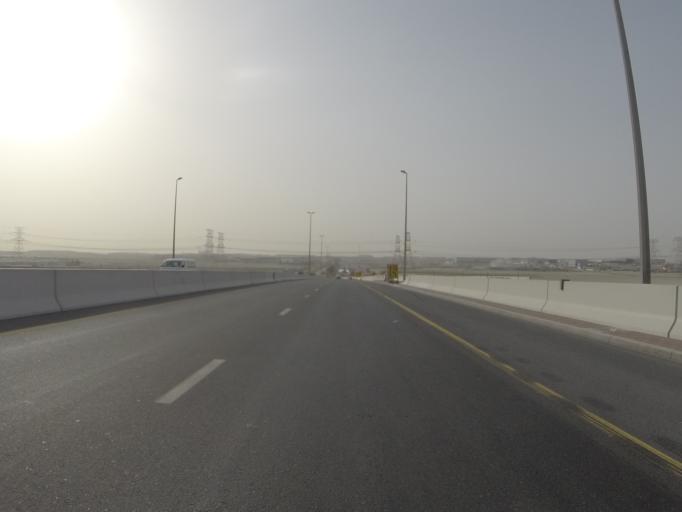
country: AE
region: Dubai
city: Dubai
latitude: 24.9577
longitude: 55.1003
